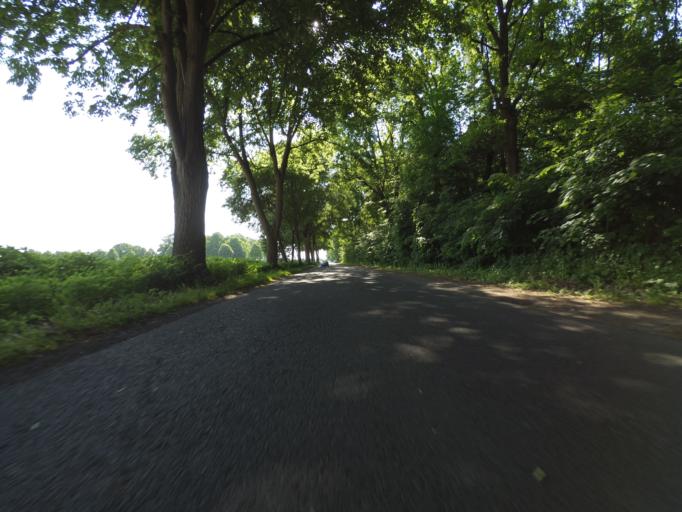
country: DE
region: Lower Saxony
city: Burgdorf
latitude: 52.4187
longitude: 10.0107
